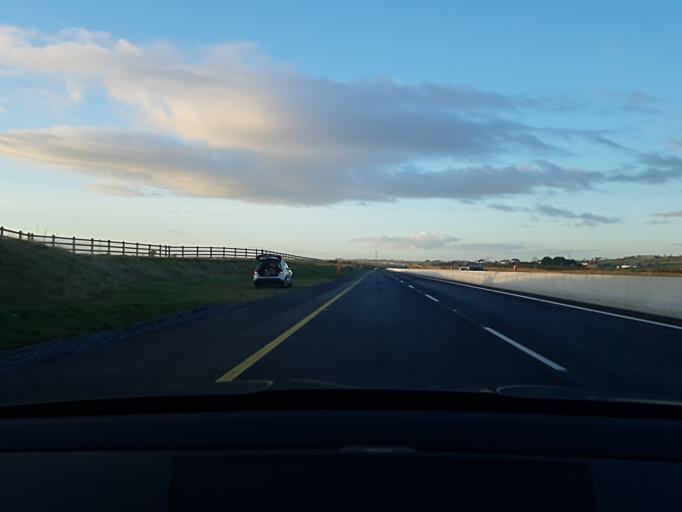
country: IE
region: Connaught
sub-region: County Galway
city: Athenry
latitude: 53.3732
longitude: -8.7928
